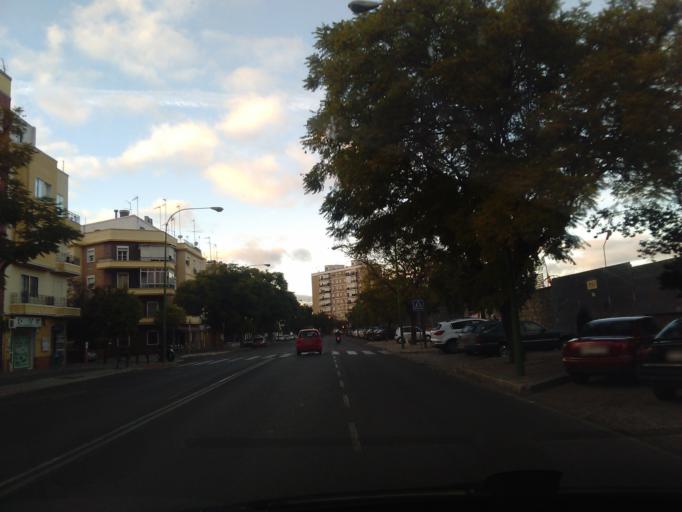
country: ES
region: Andalusia
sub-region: Provincia de Sevilla
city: Sevilla
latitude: 37.3884
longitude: -5.9656
